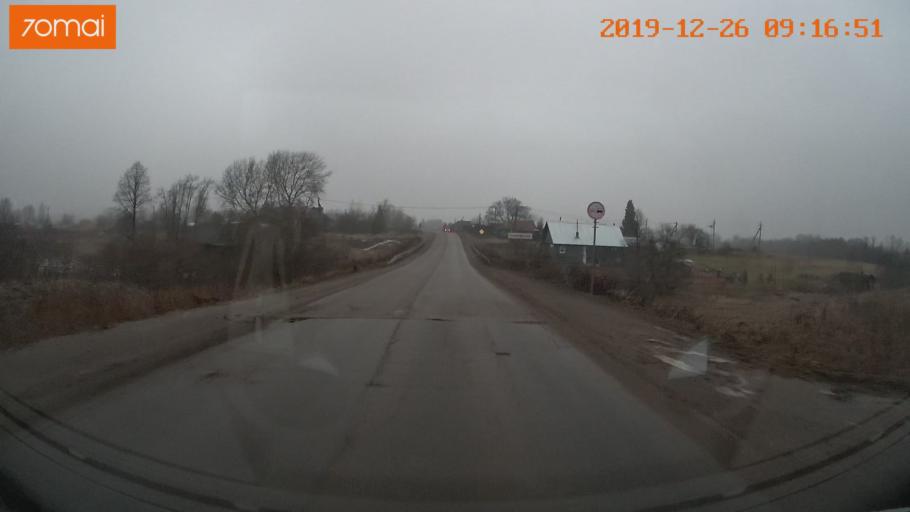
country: RU
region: Vologda
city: Gryazovets
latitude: 58.9234
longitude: 40.2393
